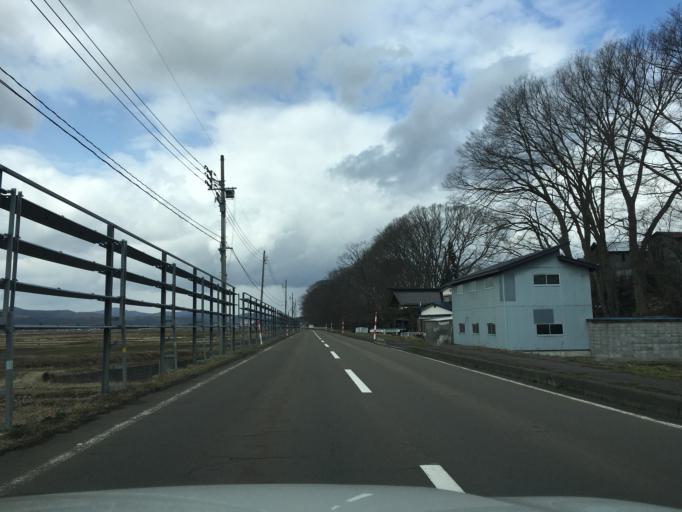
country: JP
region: Akita
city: Takanosu
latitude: 40.1438
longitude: 140.3471
